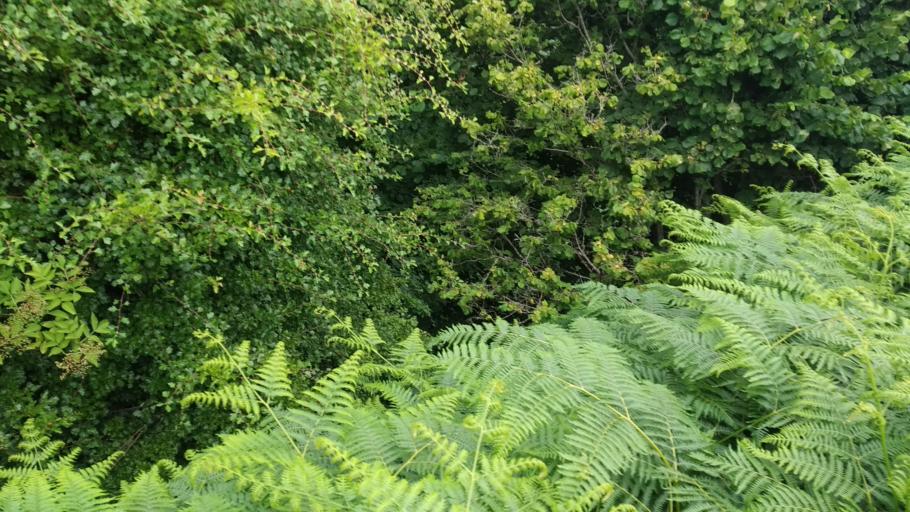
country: DK
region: South Denmark
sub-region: Vejle Kommune
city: Brejning
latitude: 55.6694
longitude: 9.6614
